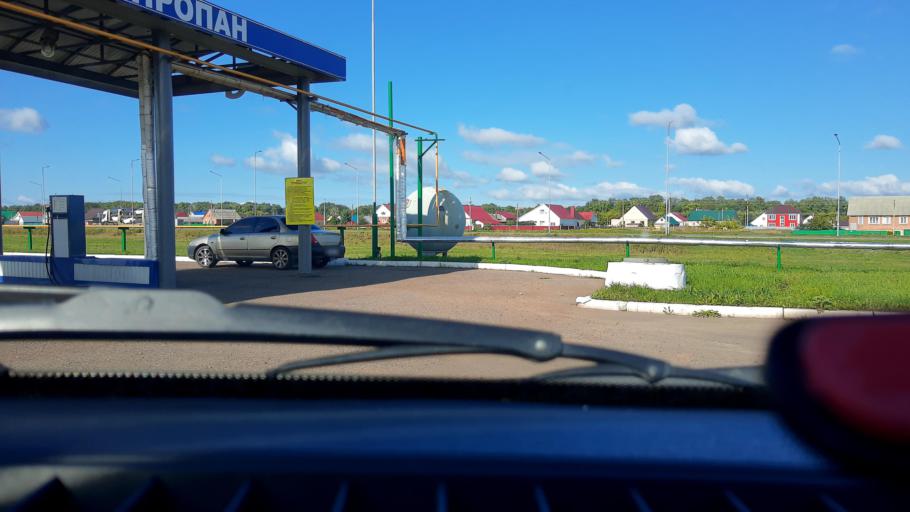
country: RU
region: Bashkortostan
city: Zirgan
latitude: 53.2476
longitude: 55.9190
